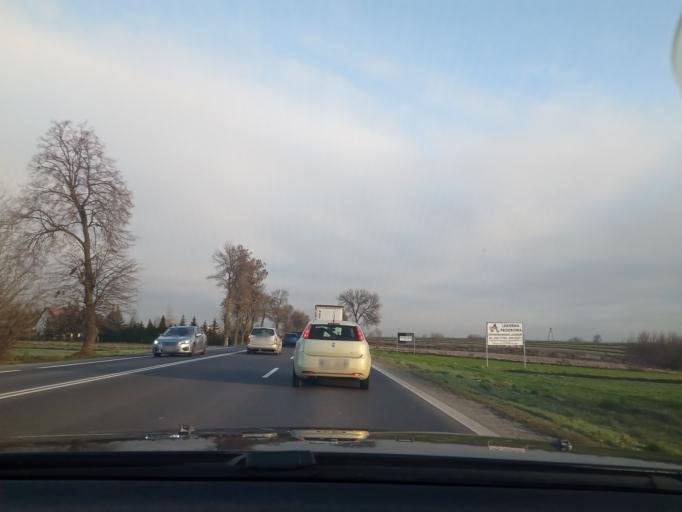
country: PL
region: Lesser Poland Voivodeship
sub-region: Powiat miechowski
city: Miechow
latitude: 50.3010
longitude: 20.0361
